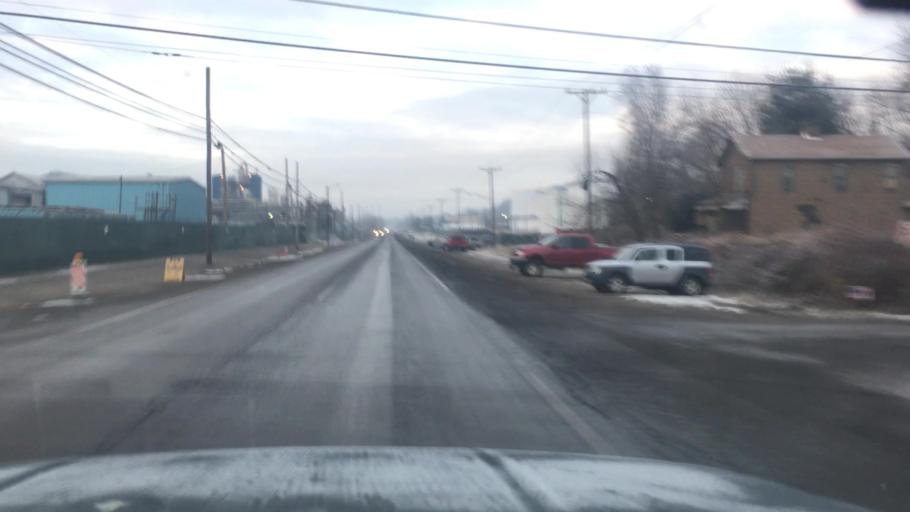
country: US
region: Pennsylvania
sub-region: Allegheny County
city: Elizabeth
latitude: 40.2679
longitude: -79.9032
